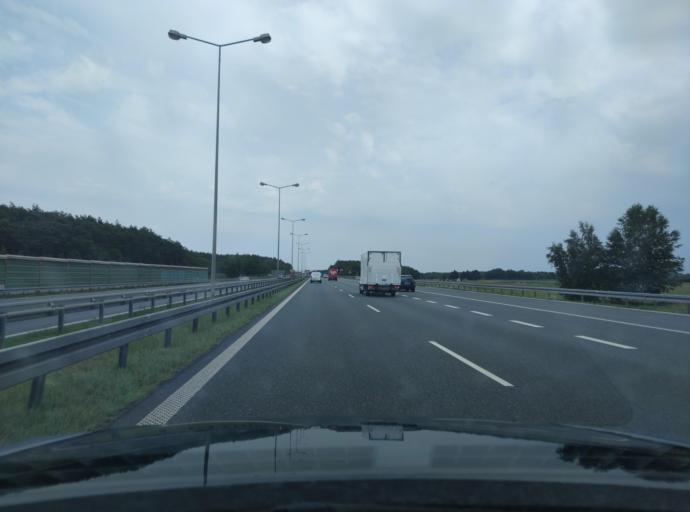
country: PL
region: Opole Voivodeship
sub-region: Powiat krapkowicki
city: Gogolin
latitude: 50.4864
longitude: 17.9951
